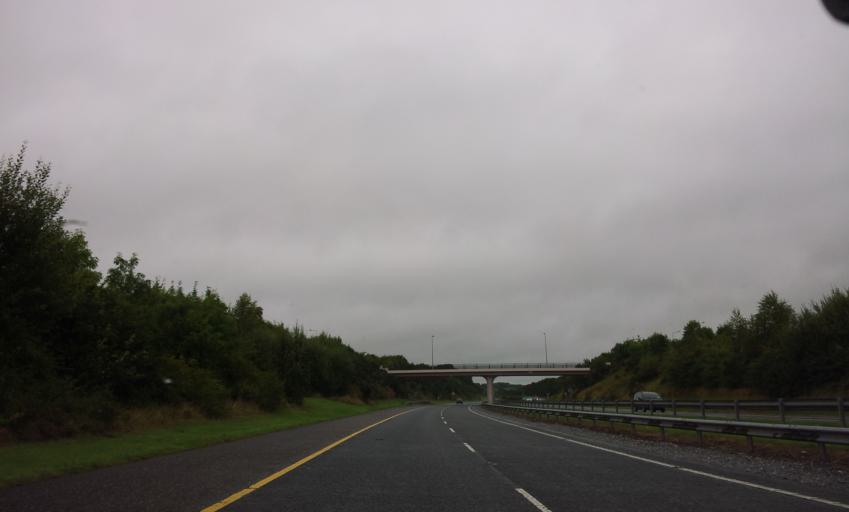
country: IE
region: Munster
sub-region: County Cork
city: Watergrasshill
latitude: 51.9534
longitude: -8.3902
